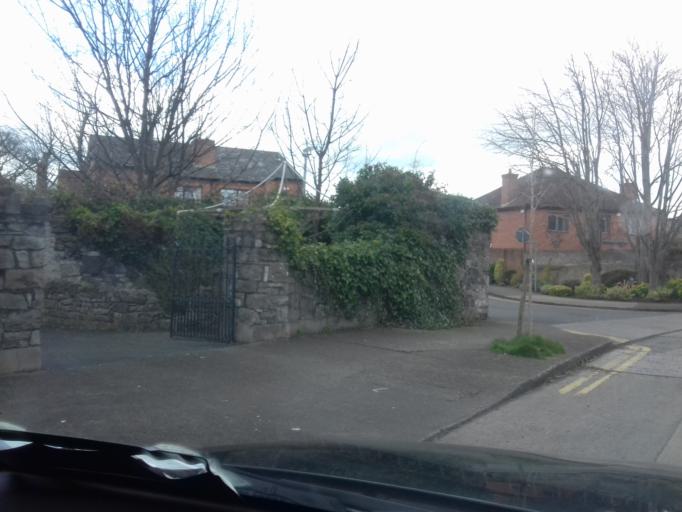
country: IE
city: Donnycarney
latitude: 53.3644
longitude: -6.2208
